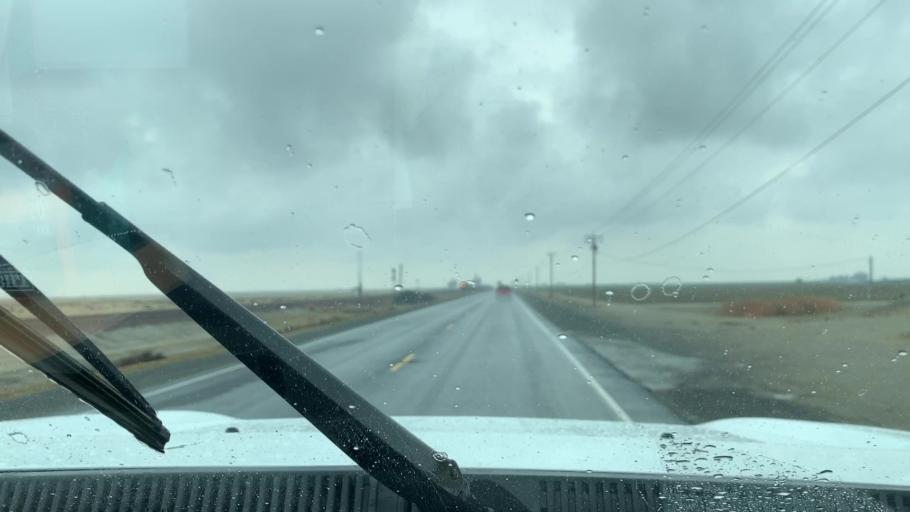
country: US
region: California
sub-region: Tulare County
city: Alpaugh
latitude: 35.9740
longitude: -119.4656
